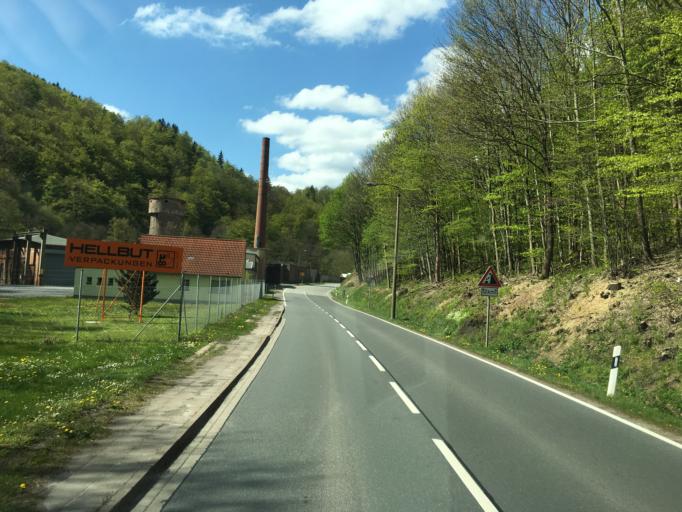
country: DE
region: Thuringia
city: Ilfeld
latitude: 51.5871
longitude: 10.7851
